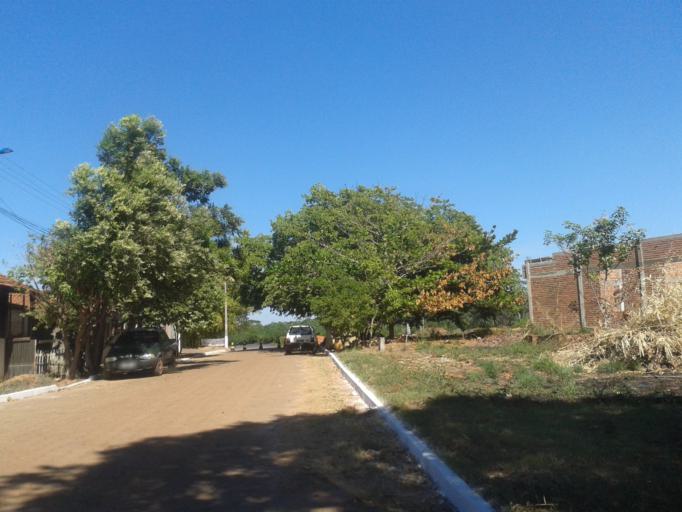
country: BR
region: Goias
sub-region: Sao Miguel Do Araguaia
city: Sao Miguel do Araguaia
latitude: -13.2178
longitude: -50.5760
